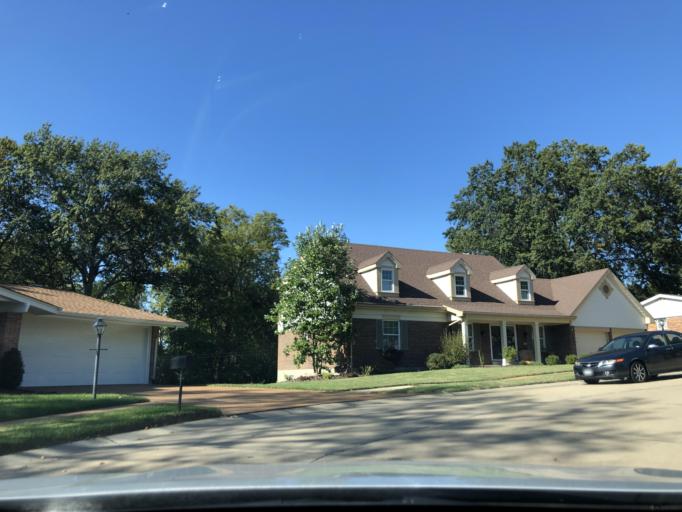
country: US
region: Missouri
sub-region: Saint Louis County
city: Concord
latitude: 38.5038
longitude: -90.3737
